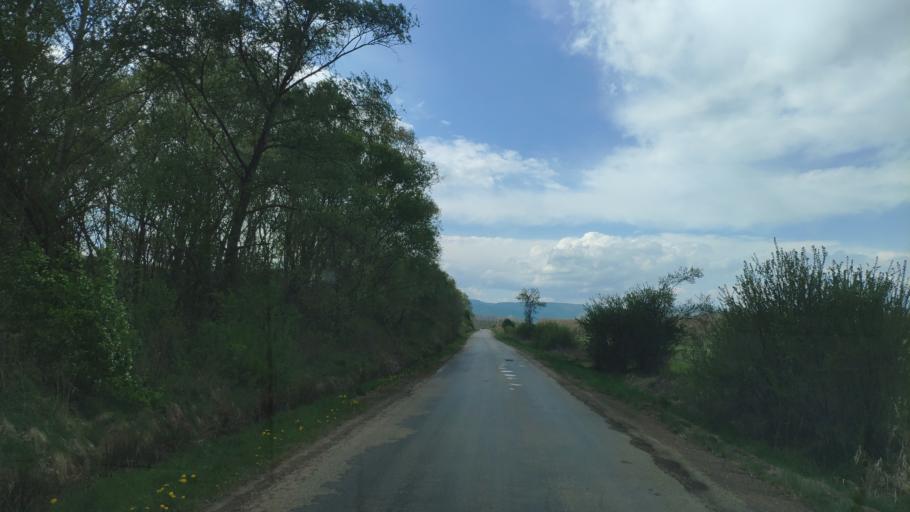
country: SK
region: Kosicky
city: Moldava nad Bodvou
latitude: 48.5607
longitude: 20.9544
